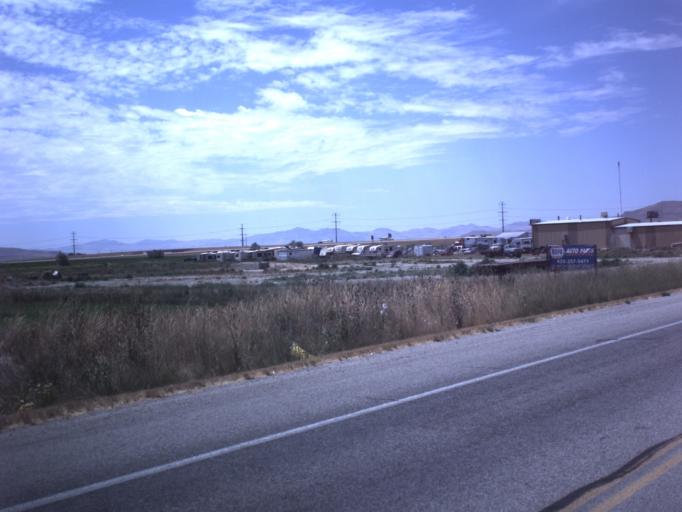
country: US
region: Utah
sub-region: Box Elder County
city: Tremonton
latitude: 41.7113
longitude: -112.1845
